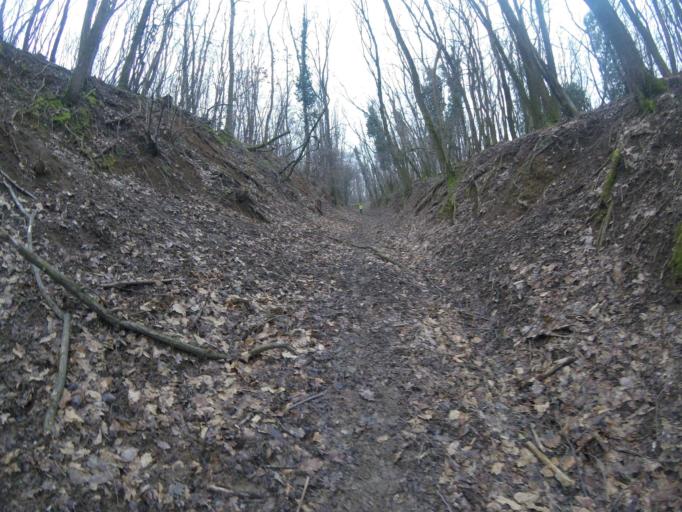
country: HU
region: Baranya
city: Mecseknadasd
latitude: 46.1387
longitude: 18.5212
